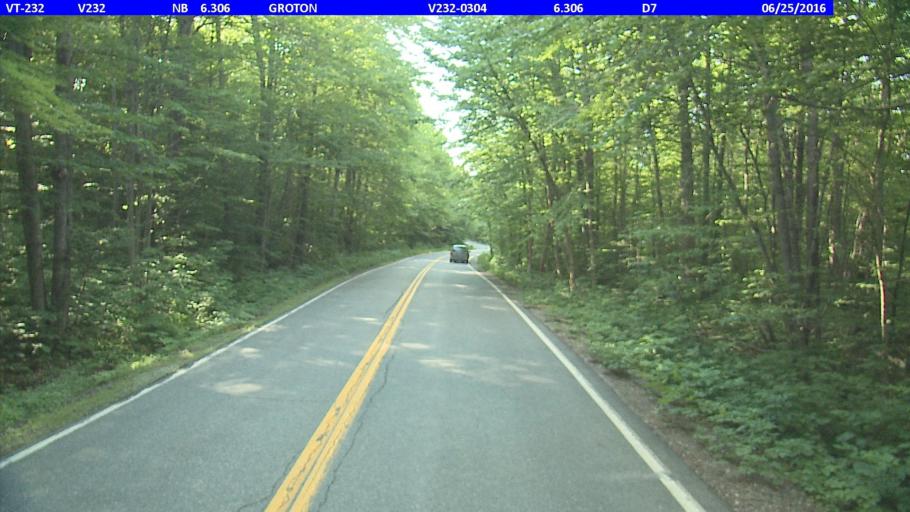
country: US
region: Vermont
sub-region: Washington County
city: Barre
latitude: 44.2861
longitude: -72.2972
